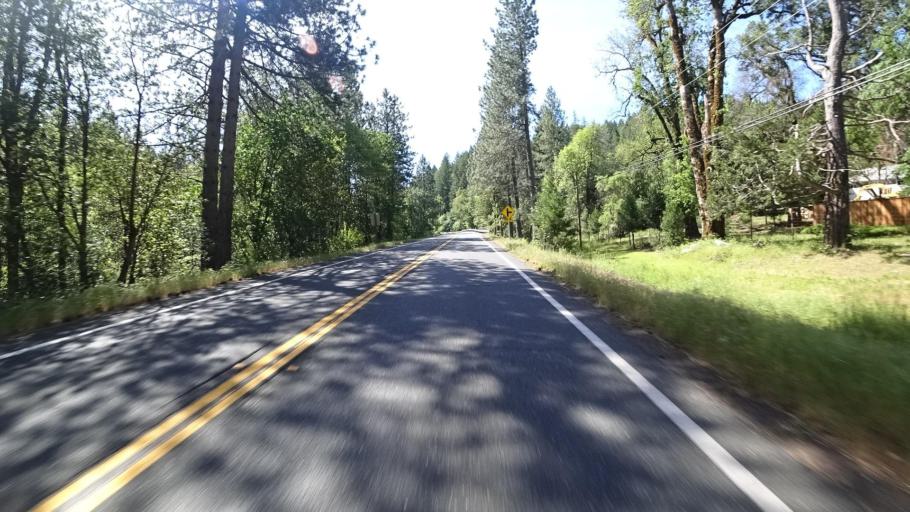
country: US
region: California
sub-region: Lake County
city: Cobb
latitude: 38.8182
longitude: -122.7152
